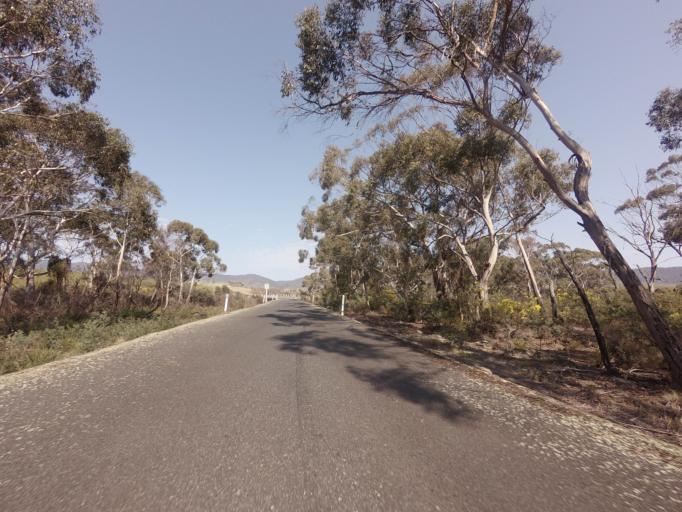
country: AU
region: Tasmania
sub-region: Northern Midlands
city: Evandale
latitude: -41.8159
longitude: 147.7537
